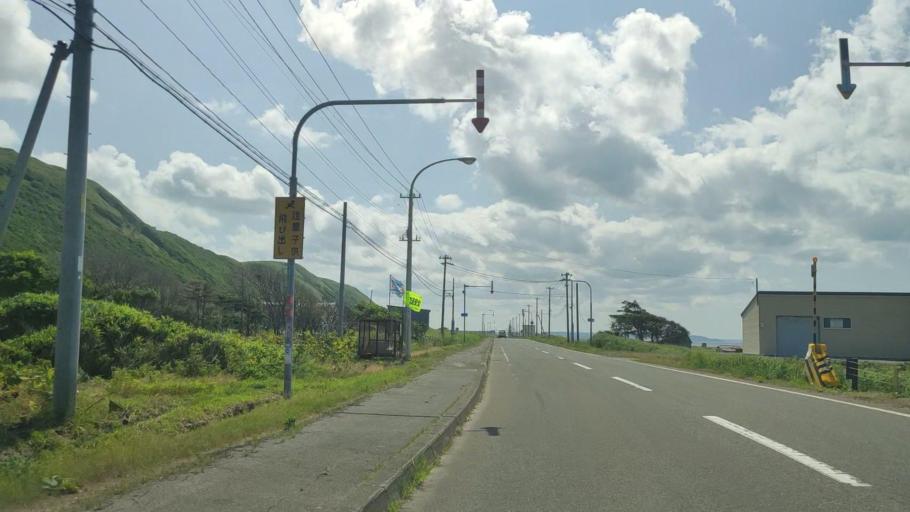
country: JP
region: Hokkaido
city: Wakkanai
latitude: 45.4051
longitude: 141.6359
